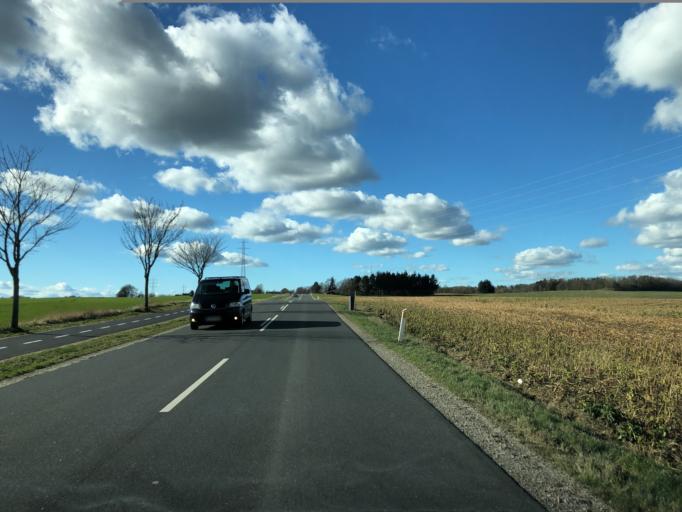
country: DK
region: Central Jutland
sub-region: Favrskov Kommune
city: Hinnerup
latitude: 56.2808
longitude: 10.0326
